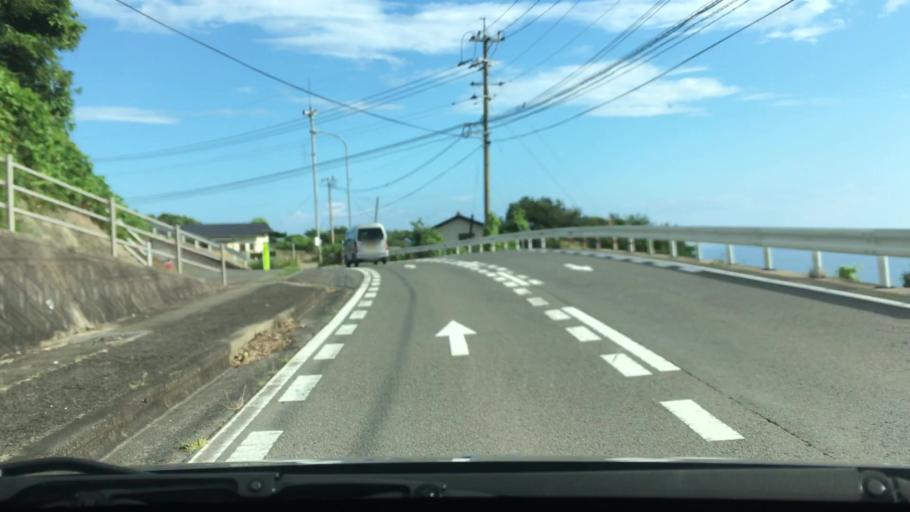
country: JP
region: Nagasaki
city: Togitsu
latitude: 32.8546
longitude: 129.6867
